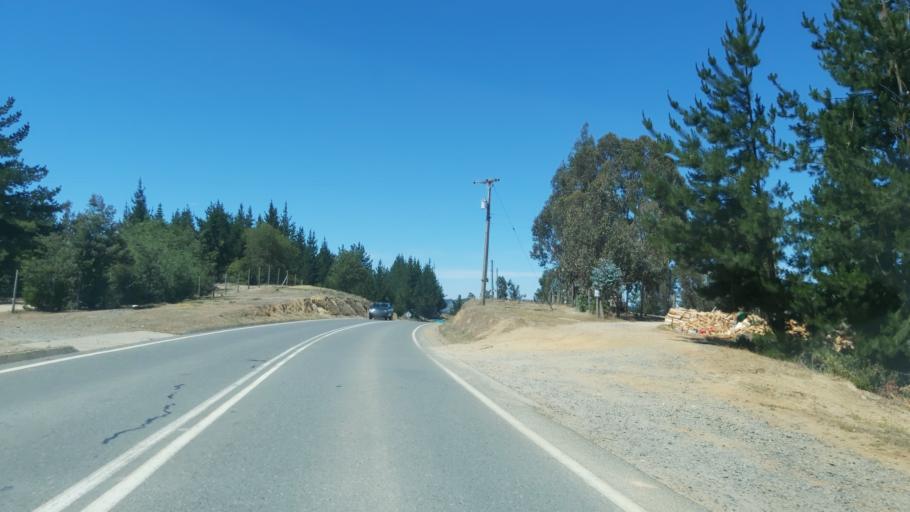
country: CL
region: Maule
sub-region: Provincia de Talca
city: Talca
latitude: -34.9705
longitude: -71.9639
